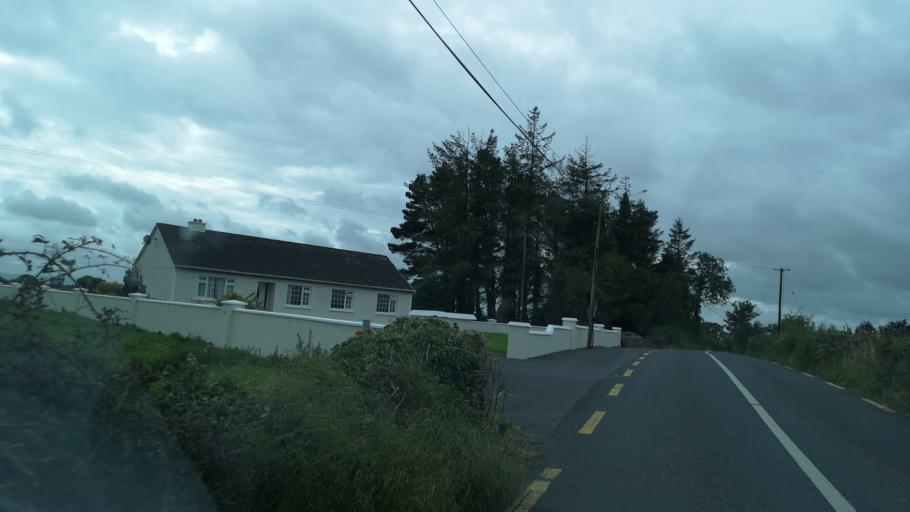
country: IE
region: Connaught
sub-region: County Galway
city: Loughrea
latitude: 53.2807
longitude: -8.6283
